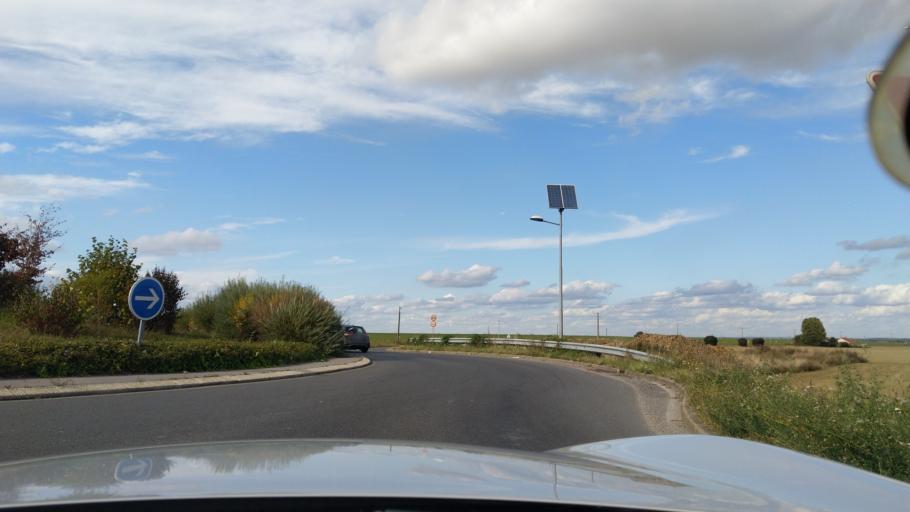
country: FR
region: Ile-de-France
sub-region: Departement de Seine-et-Marne
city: Monthyon
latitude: 49.0194
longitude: 2.8259
